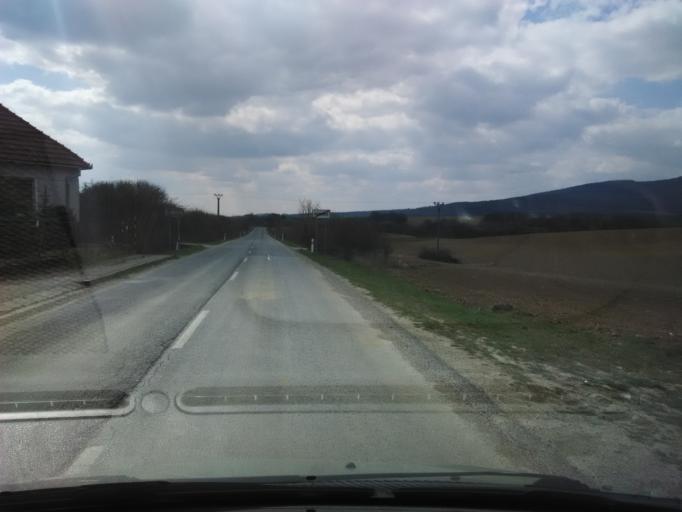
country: SK
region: Nitriansky
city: Zlate Moravce
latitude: 48.4250
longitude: 18.3232
